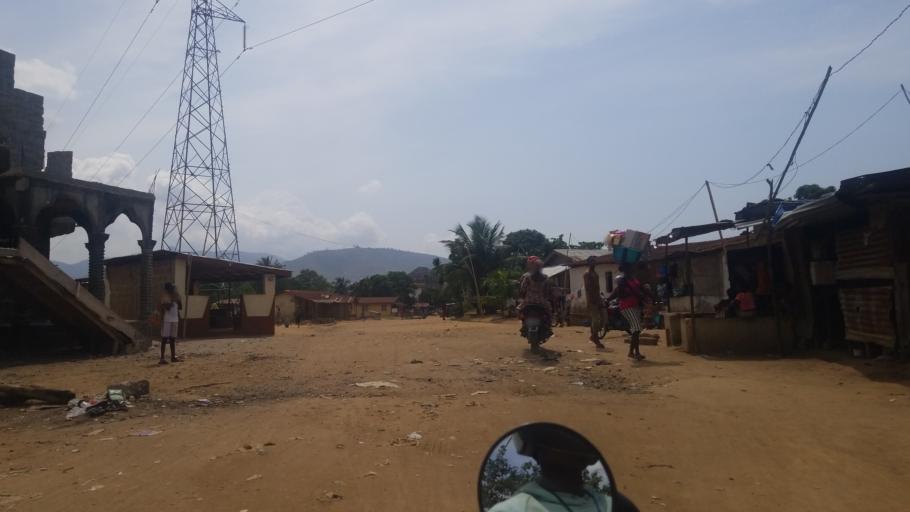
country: SL
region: Western Area
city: Waterloo
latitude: 8.3259
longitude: -13.0482
